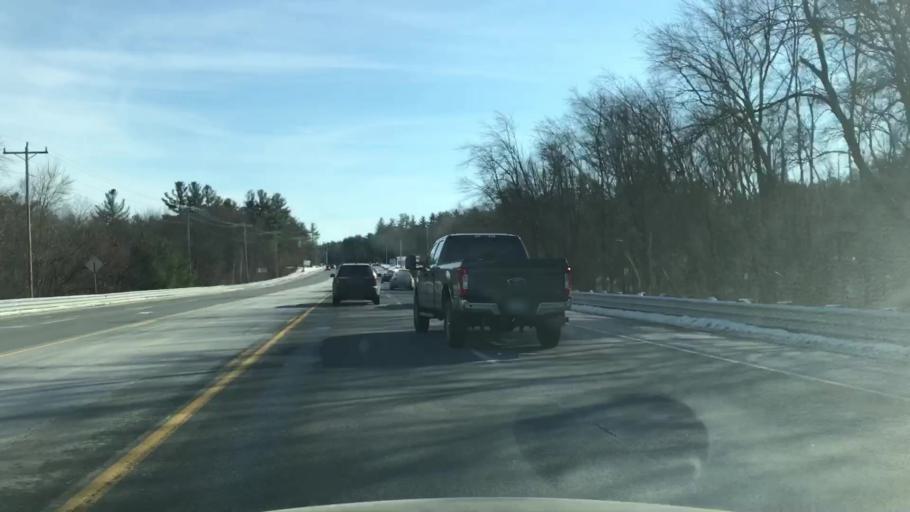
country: US
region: New Hampshire
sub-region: Hillsborough County
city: Milford
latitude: 42.8203
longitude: -71.6042
